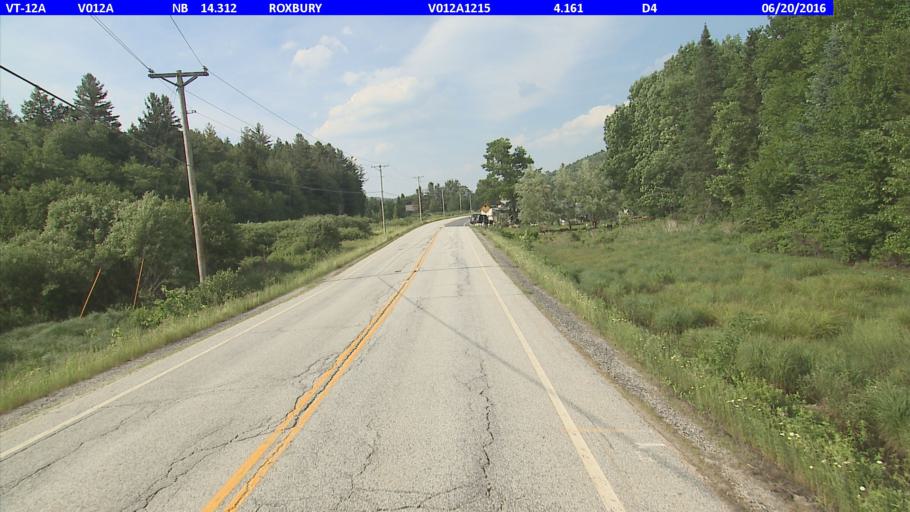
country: US
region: Vermont
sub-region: Washington County
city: Northfield
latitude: 44.0856
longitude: -72.7358
